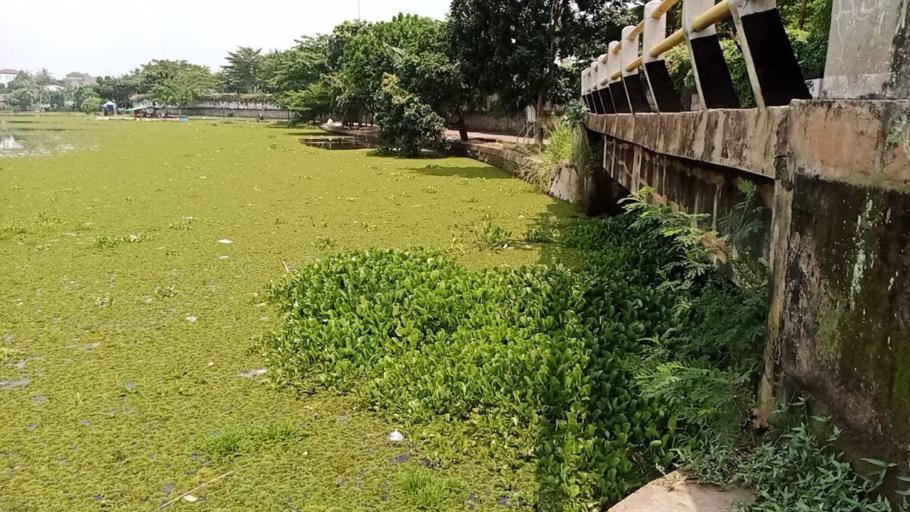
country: ID
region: West Java
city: Sawangan
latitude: -6.3844
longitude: 106.7527
